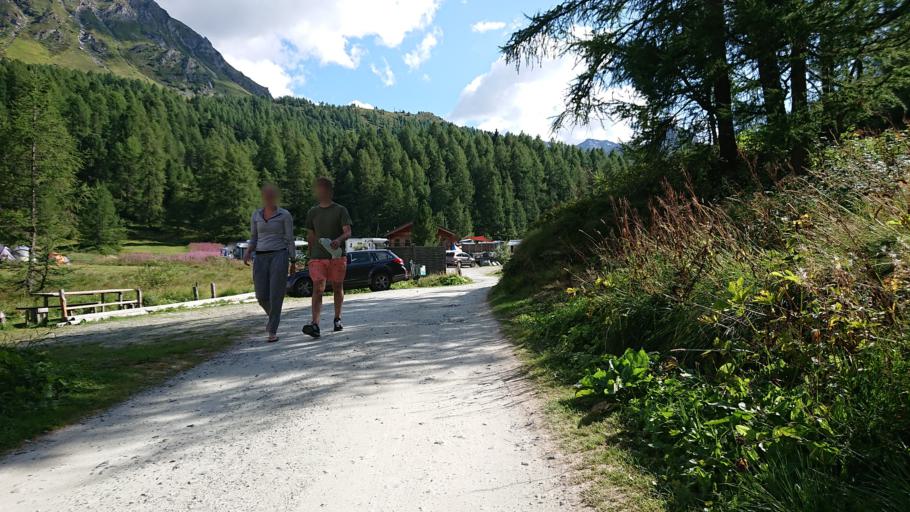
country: CH
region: Grisons
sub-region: Maloja District
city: Silvaplana
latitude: 46.4065
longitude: 9.7106
